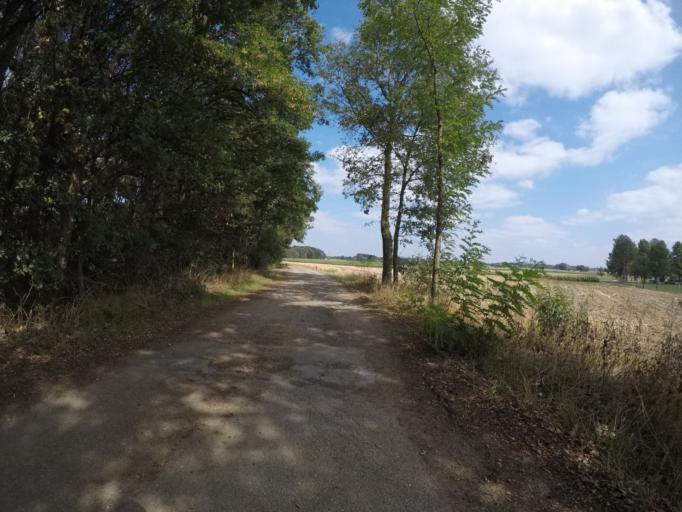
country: DE
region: North Rhine-Westphalia
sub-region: Regierungsbezirk Munster
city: Isselburg
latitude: 51.7987
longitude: 6.4940
